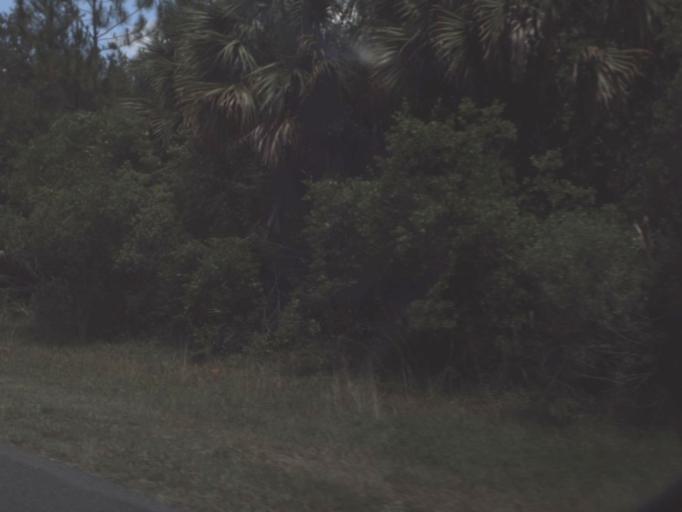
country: US
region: Florida
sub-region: Marion County
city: Silver Springs Shores
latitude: 29.2135
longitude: -81.9683
